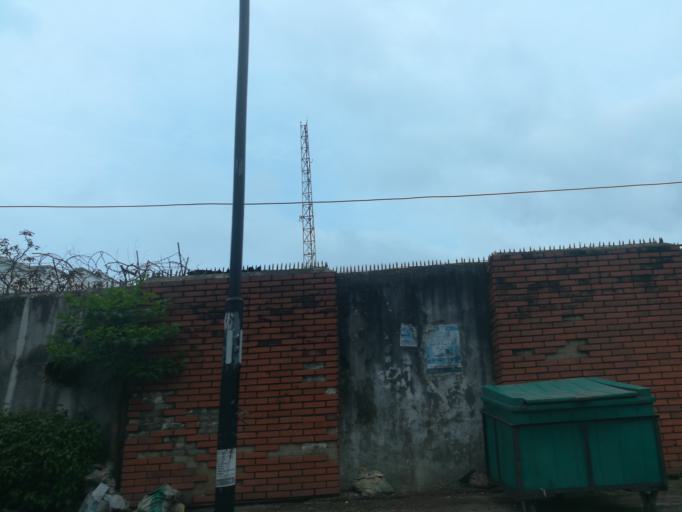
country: NG
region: Lagos
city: Oshodi
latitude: 6.5735
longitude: 3.3547
